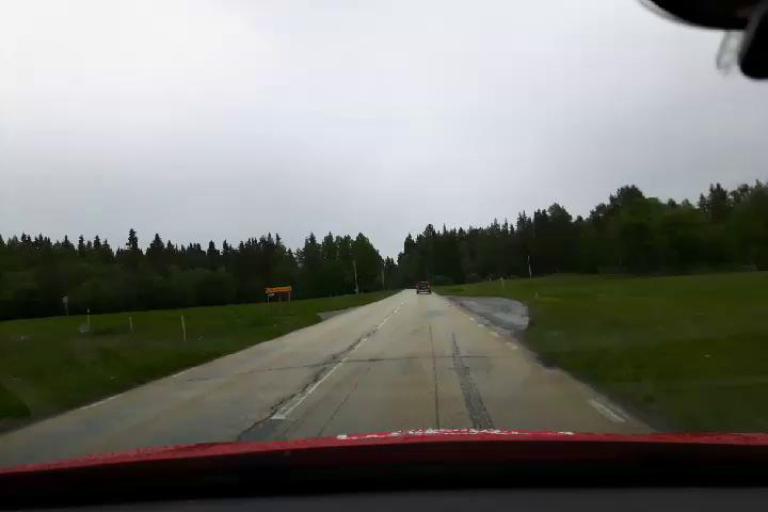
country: SE
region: Jaemtland
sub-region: Bergs Kommun
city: Hoverberg
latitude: 62.7822
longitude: 14.4340
